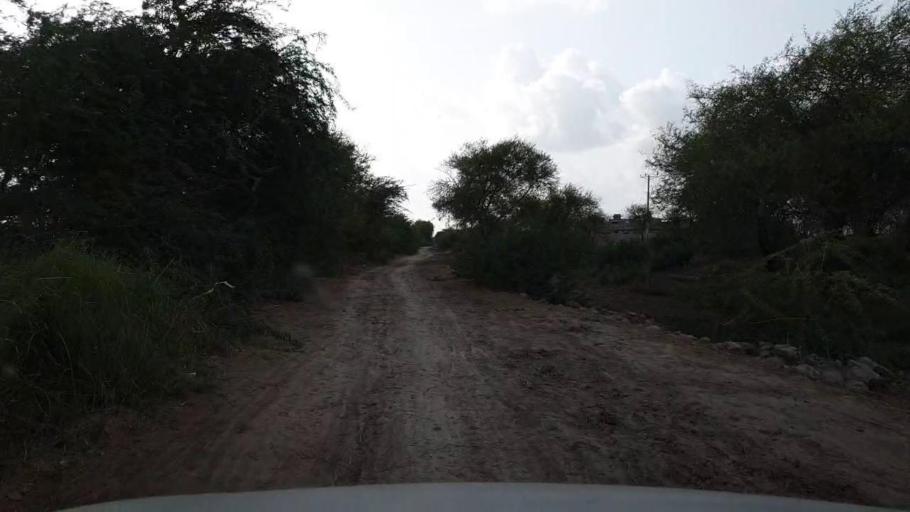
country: PK
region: Sindh
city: Kario
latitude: 24.7609
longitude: 68.6048
